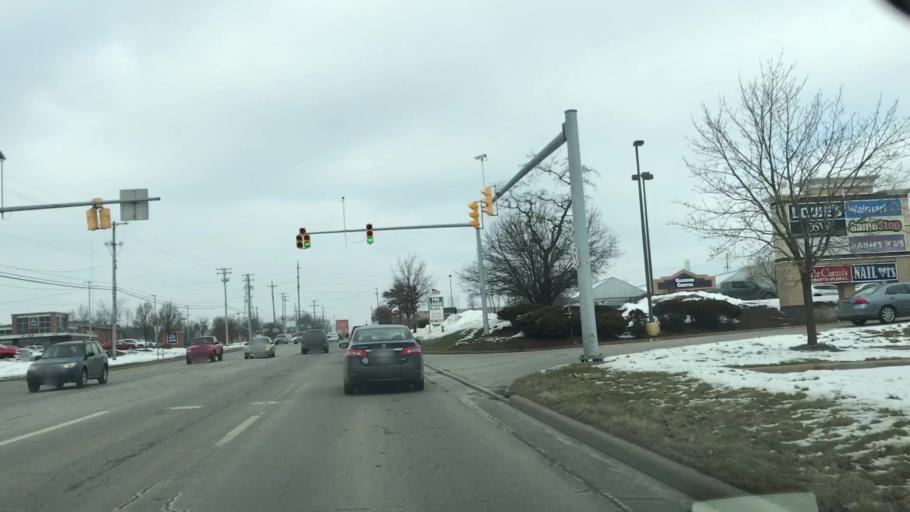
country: US
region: Ohio
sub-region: Mahoning County
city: Poland
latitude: 41.0299
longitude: -80.6345
